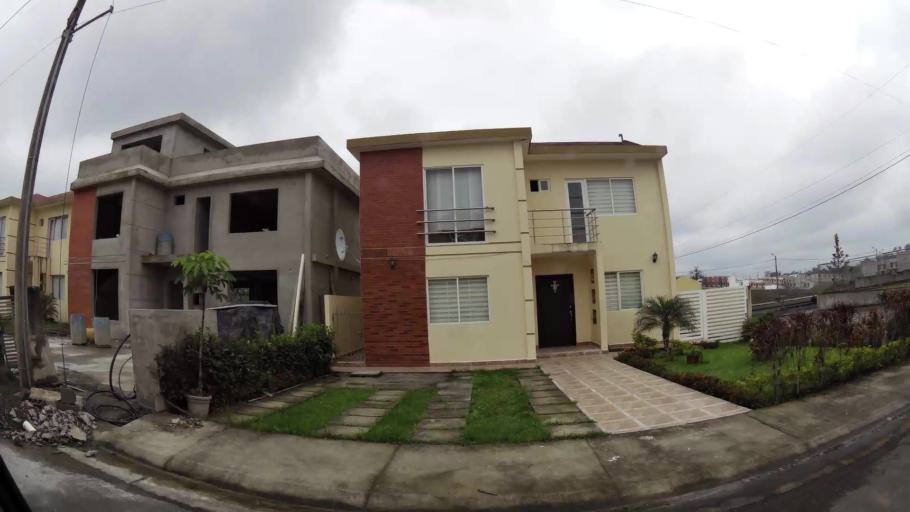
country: EC
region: Santo Domingo de los Tsachilas
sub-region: Canton Santo Domingo de los Colorados
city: Santo Domingo de los Colorados
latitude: -0.2543
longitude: -79.1380
